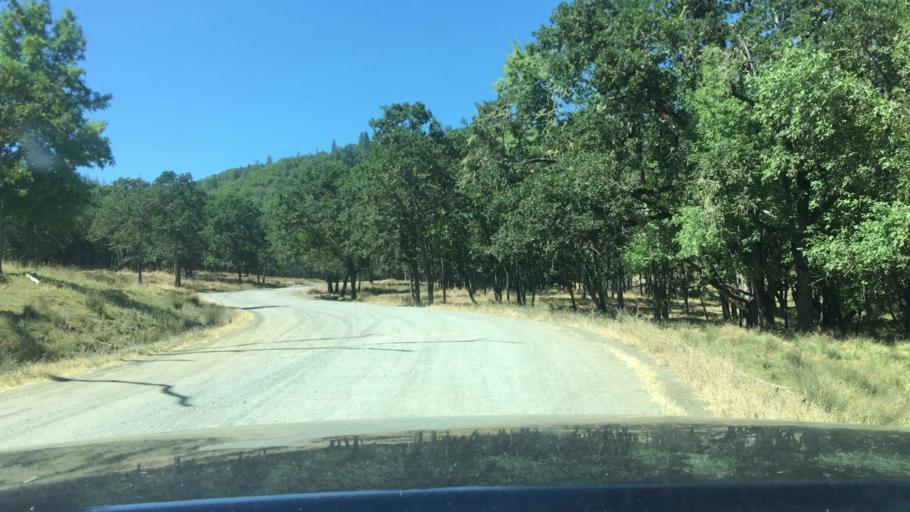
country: US
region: Oregon
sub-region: Douglas County
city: Winston
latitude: 43.1364
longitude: -123.4400
